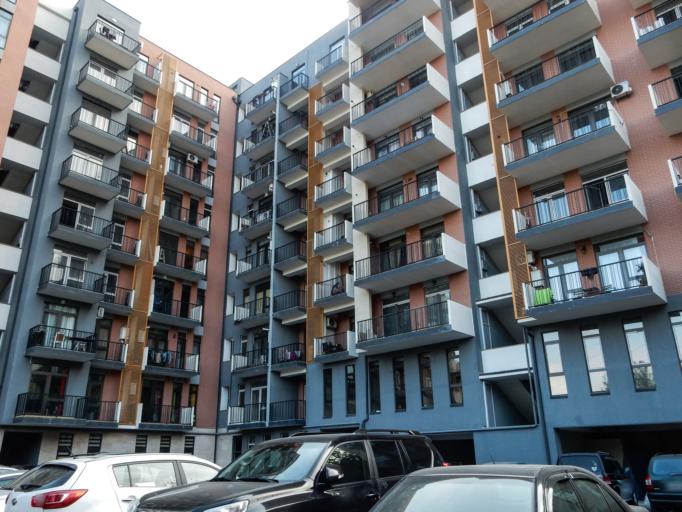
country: GE
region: T'bilisi
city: Tbilisi
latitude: 41.6816
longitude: 44.8221
